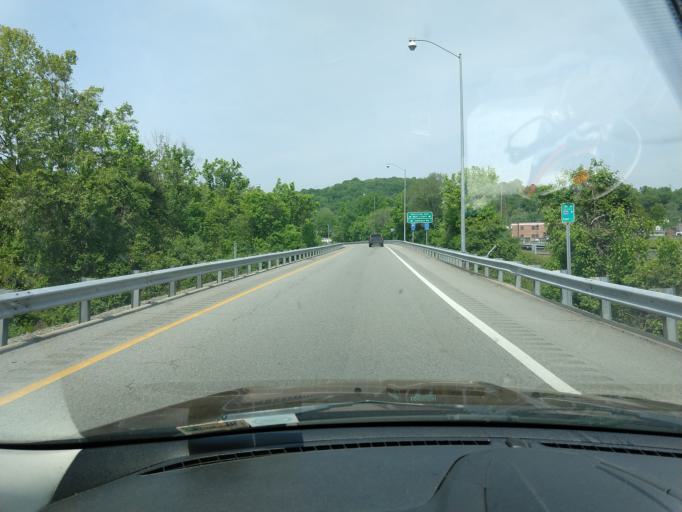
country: US
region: West Virginia
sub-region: Kanawha County
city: South Charleston
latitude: 38.3607
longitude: -81.7120
